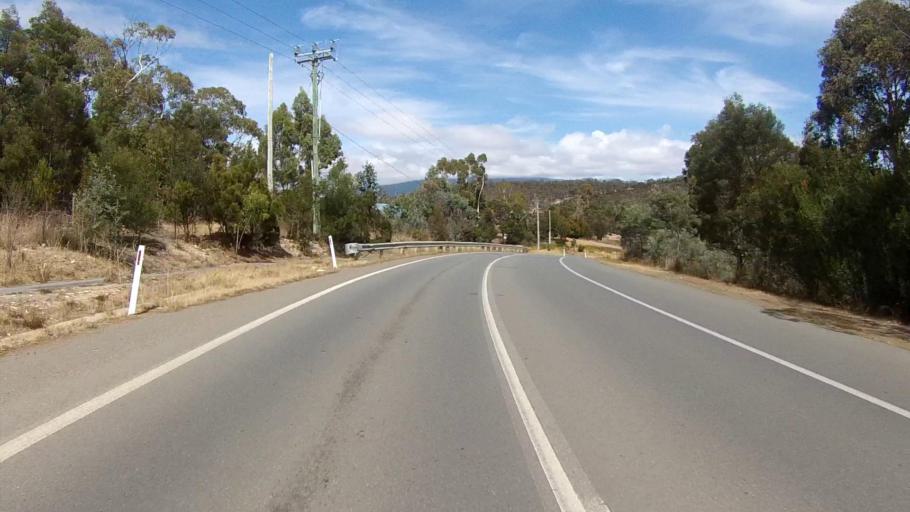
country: AU
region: Tasmania
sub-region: Clarence
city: Lindisfarne
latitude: -42.8234
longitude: 147.3491
